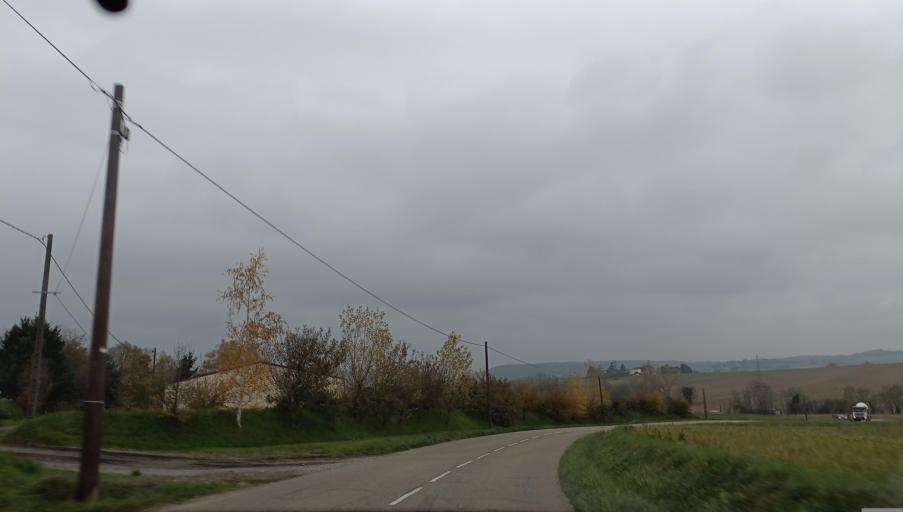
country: FR
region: Rhone-Alpes
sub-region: Departement de l'Isere
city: Serpaize
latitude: 45.5669
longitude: 4.9064
